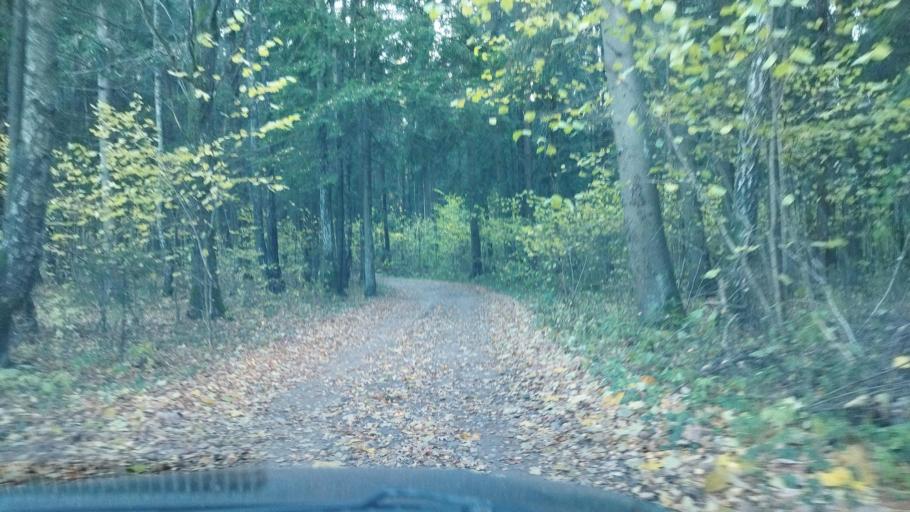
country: BY
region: Minsk
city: Slabada
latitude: 53.9915
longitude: 27.8902
